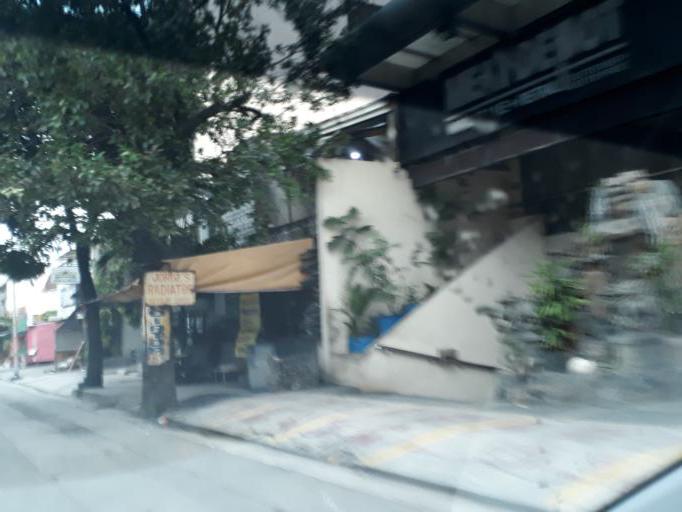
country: PH
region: Calabarzon
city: Del Monte
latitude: 14.6367
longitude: 121.0011
